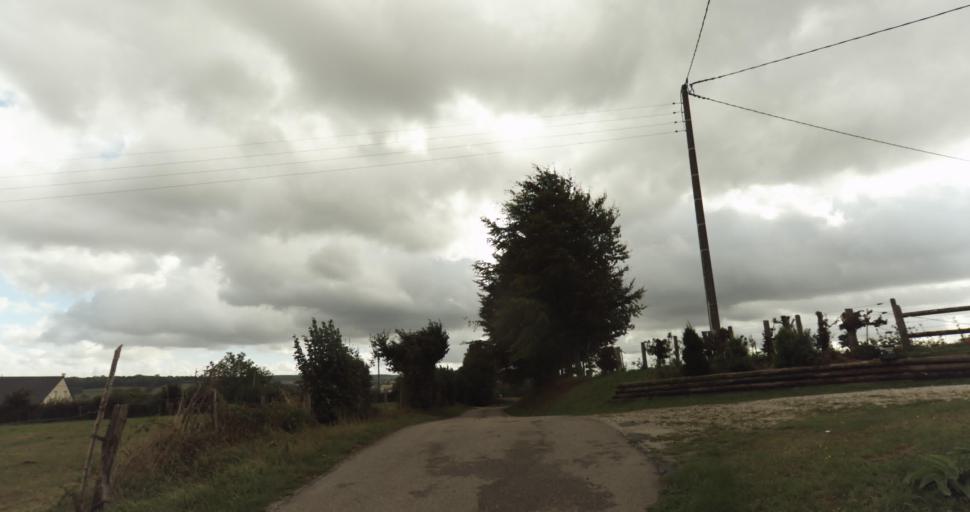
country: FR
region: Lower Normandy
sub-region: Departement de l'Orne
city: Gace
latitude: 48.8029
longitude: 0.2776
